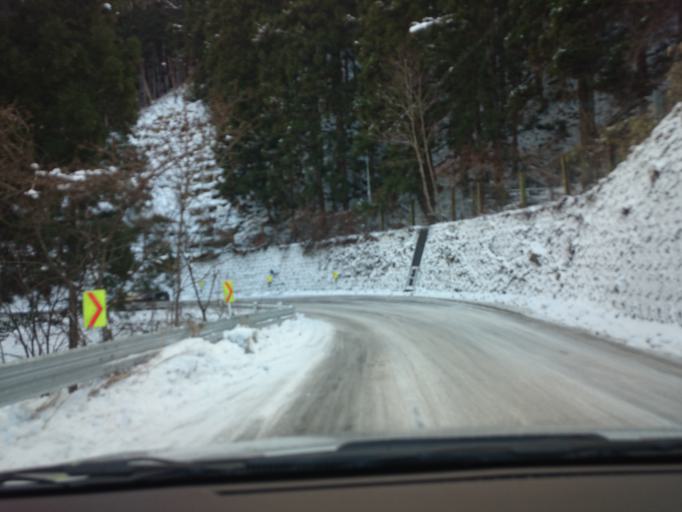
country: JP
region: Gifu
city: Gujo
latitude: 35.7398
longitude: 136.9870
